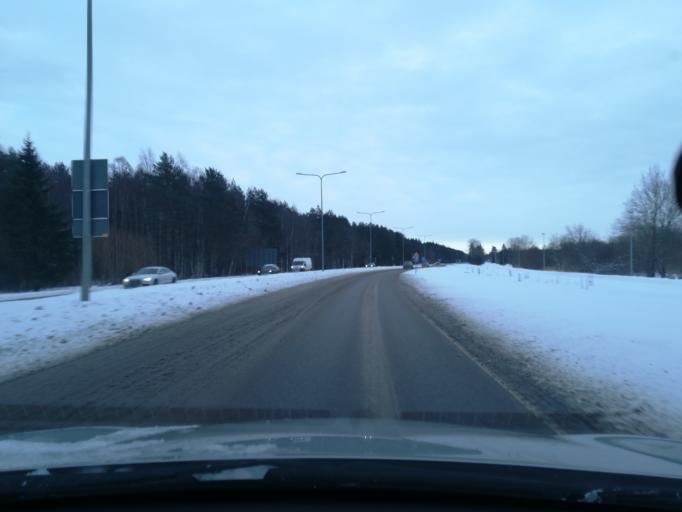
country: EE
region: Harju
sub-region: Harku vald
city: Tabasalu
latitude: 59.4369
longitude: 24.5766
